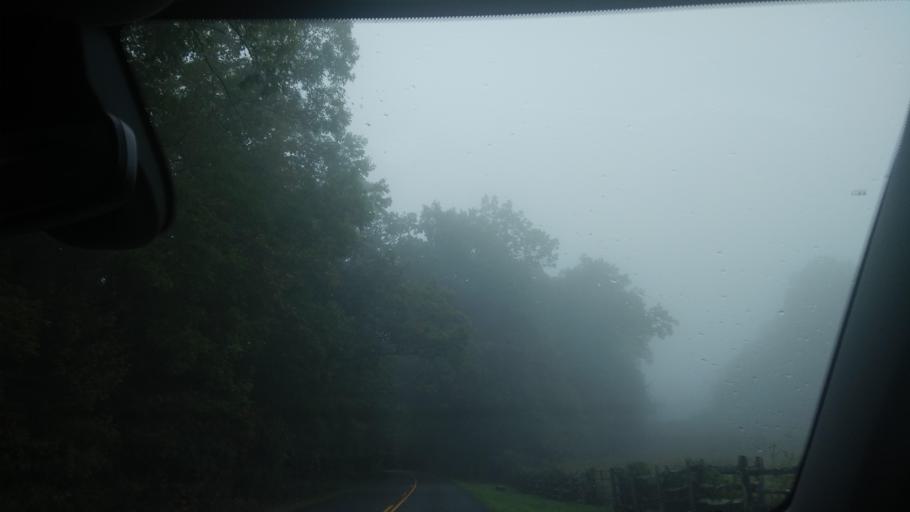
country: US
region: North Carolina
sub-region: Mitchell County
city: Spruce Pine
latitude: 35.8840
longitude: -81.9828
